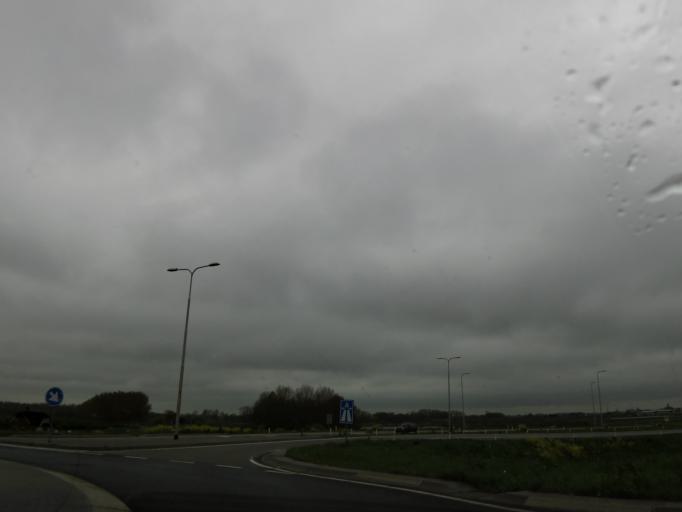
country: NL
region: Gelderland
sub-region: Gemeente Culemborg
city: Culemborg
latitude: 51.9281
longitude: 5.1630
